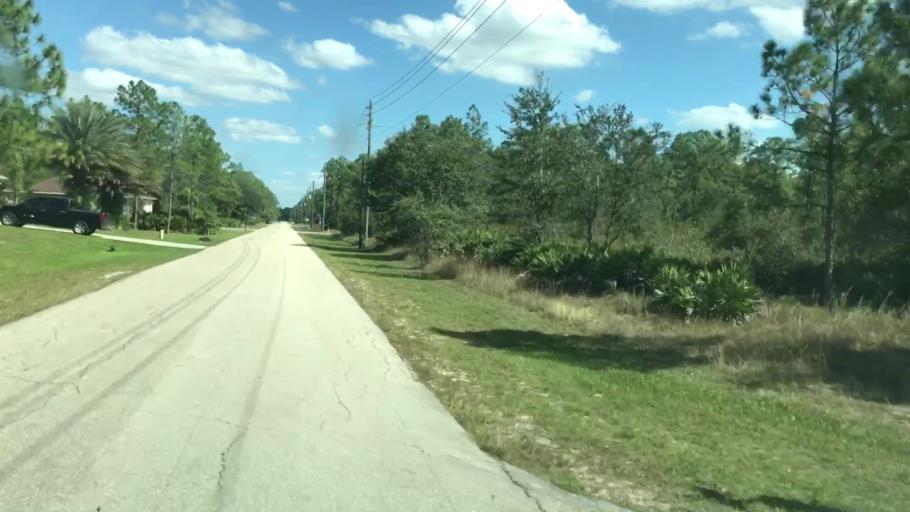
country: US
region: Florida
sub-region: Lee County
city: Alva
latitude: 26.6835
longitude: -81.5939
